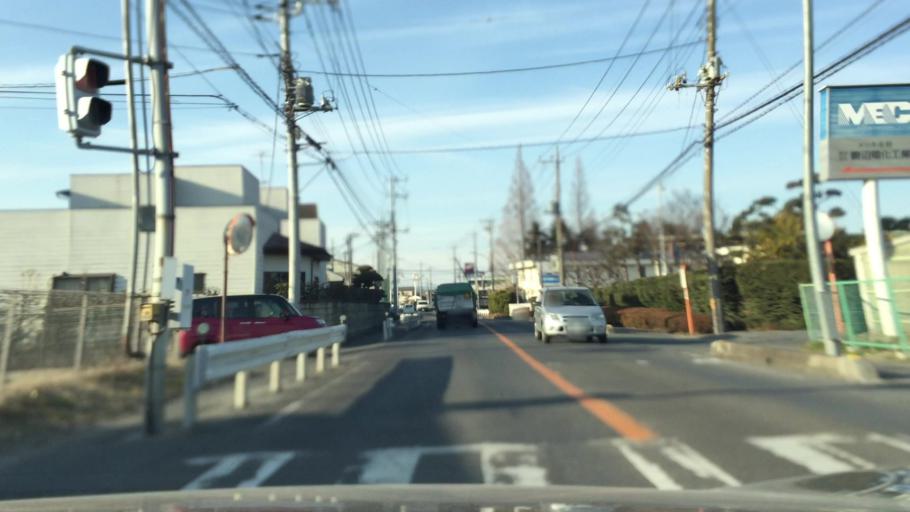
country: JP
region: Saitama
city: Menuma
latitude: 36.2124
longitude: 139.3783
